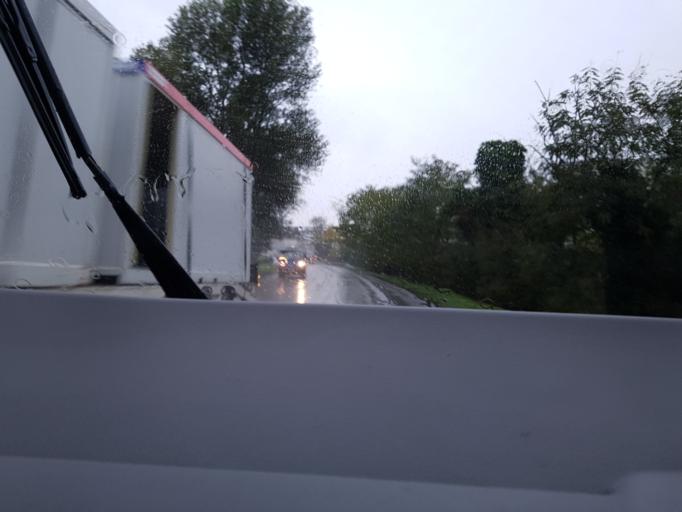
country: FR
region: Aquitaine
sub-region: Departement de la Gironde
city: Bassens
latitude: 44.9116
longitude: -0.5372
